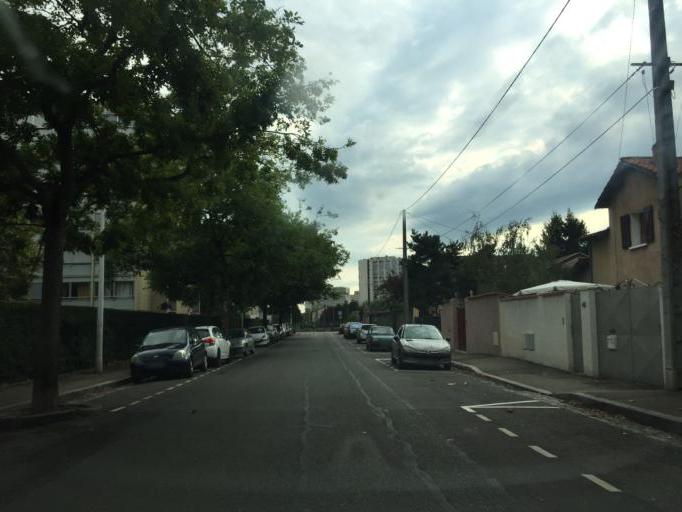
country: FR
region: Rhone-Alpes
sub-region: Departement du Rhone
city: Saint-Fons
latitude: 45.7308
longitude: 4.8793
